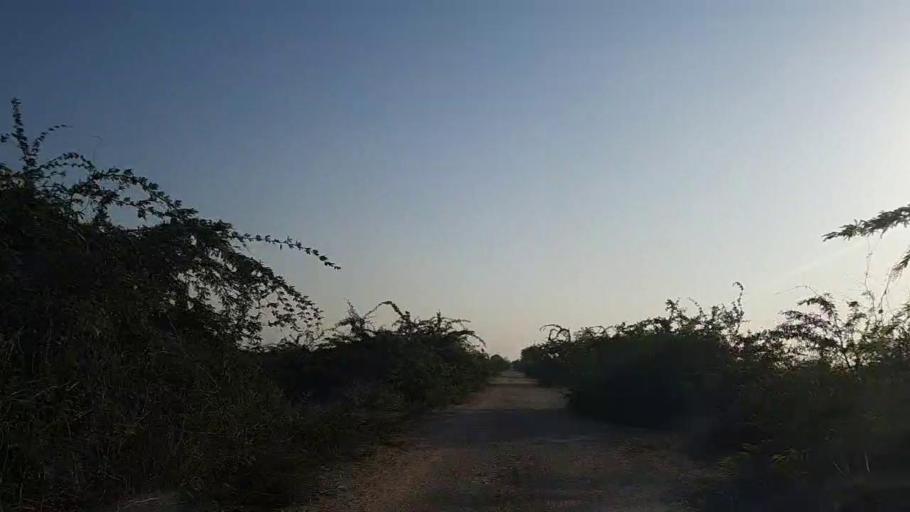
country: PK
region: Sindh
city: Jati
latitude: 24.4261
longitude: 68.1886
